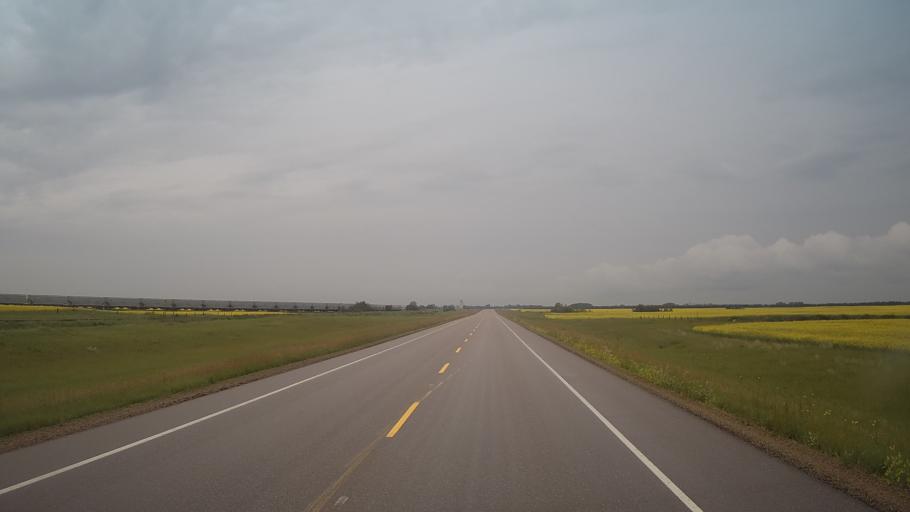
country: CA
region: Saskatchewan
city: Wilkie
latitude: 52.3026
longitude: -108.6771
